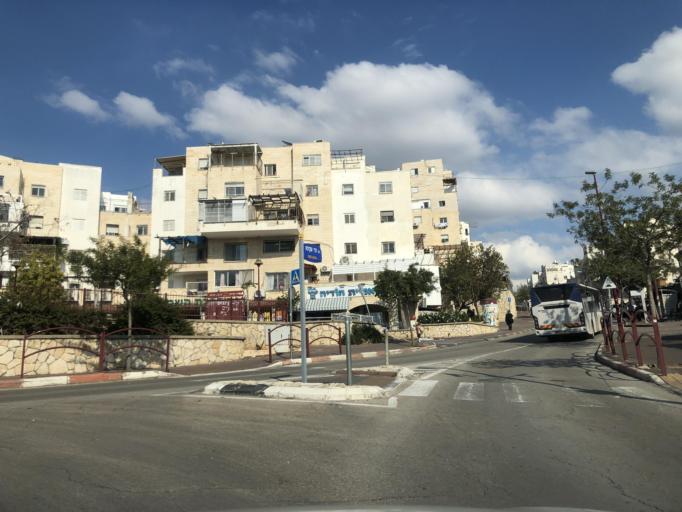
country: IL
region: Jerusalem
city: Modiin Ilit
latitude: 31.9394
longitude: 35.0385
